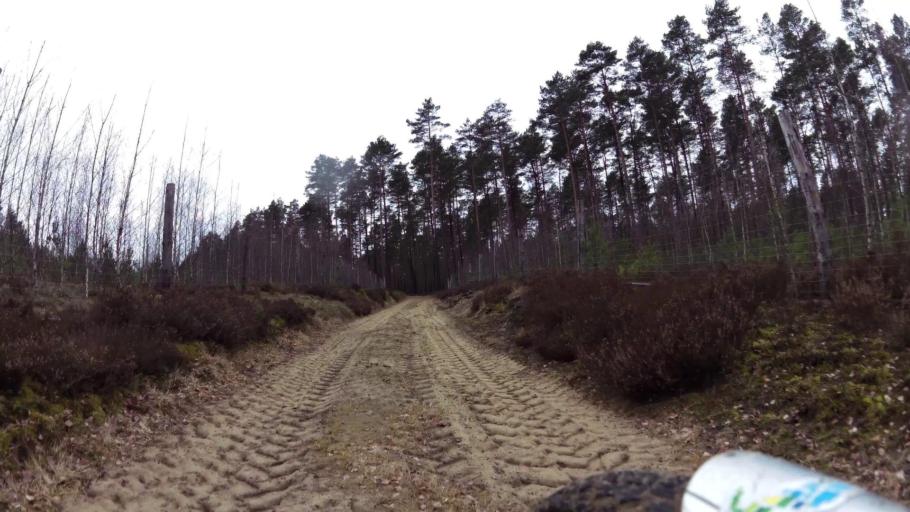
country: PL
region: Pomeranian Voivodeship
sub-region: Powiat bytowski
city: Kolczyglowy
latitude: 54.2415
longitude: 17.2726
